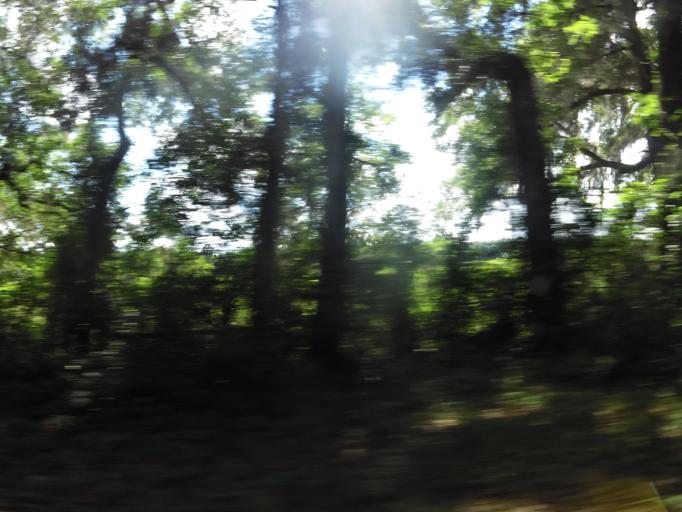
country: US
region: Florida
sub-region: Clay County
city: Keystone Heights
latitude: 29.7720
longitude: -81.8885
